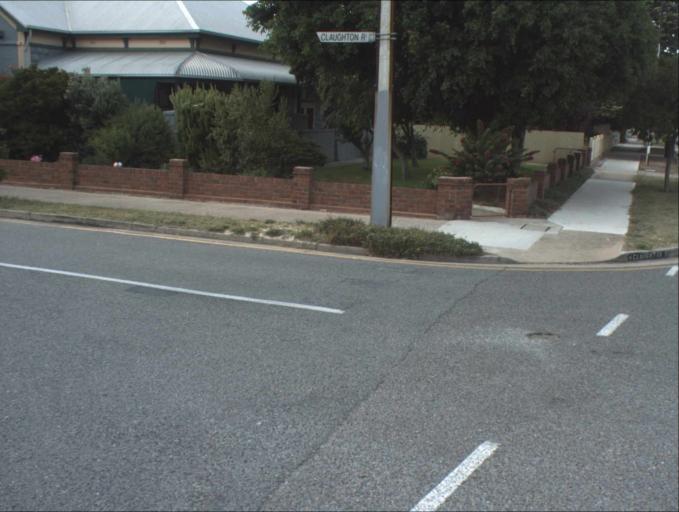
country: AU
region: South Australia
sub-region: Port Adelaide Enfield
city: Birkenhead
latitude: -34.8279
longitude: 138.4914
